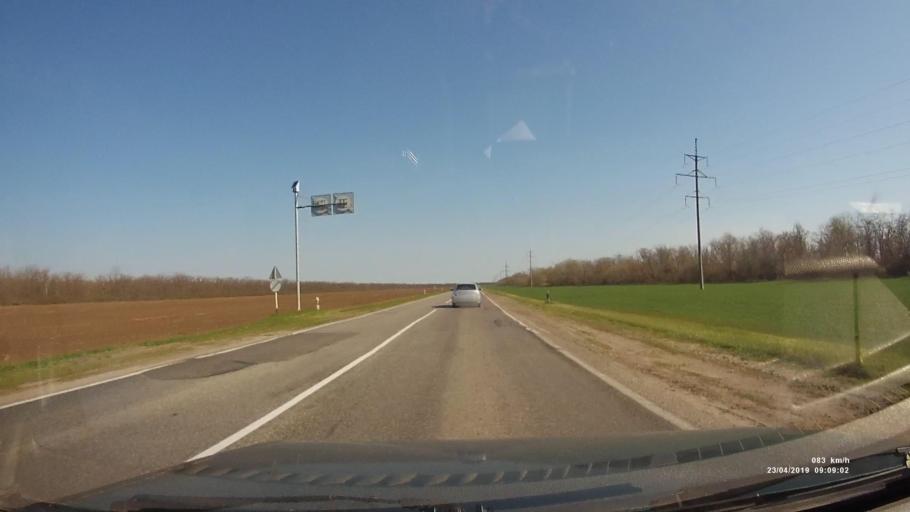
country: RU
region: Rostov
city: Sal'sk
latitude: 46.5679
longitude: 41.6130
